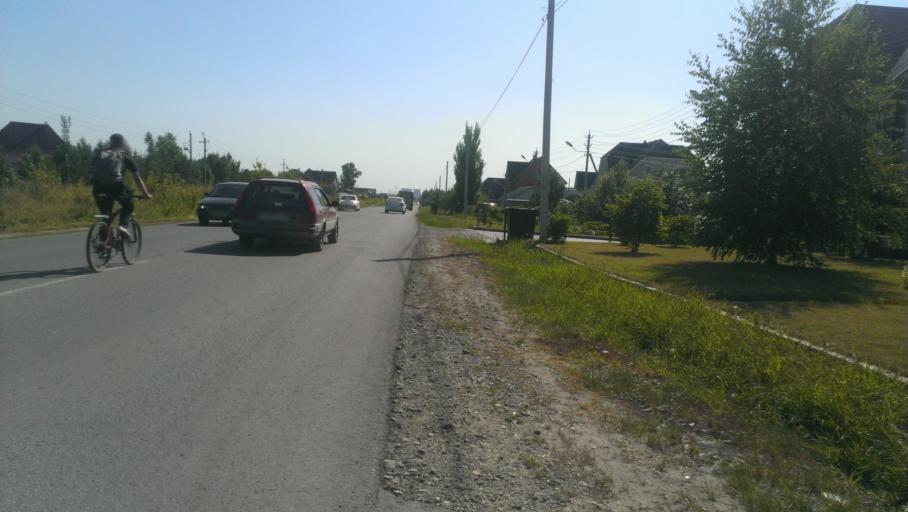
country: RU
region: Altai Krai
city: Novosilikatnyy
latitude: 53.3678
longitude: 83.6486
